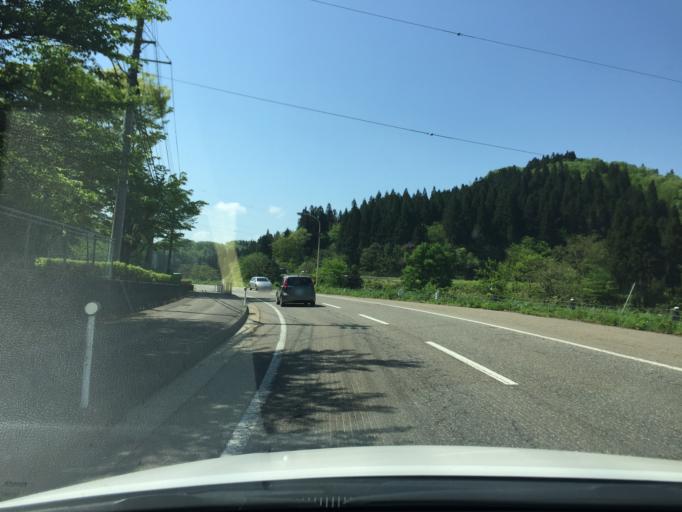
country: JP
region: Niigata
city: Kamo
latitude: 37.6140
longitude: 139.1022
